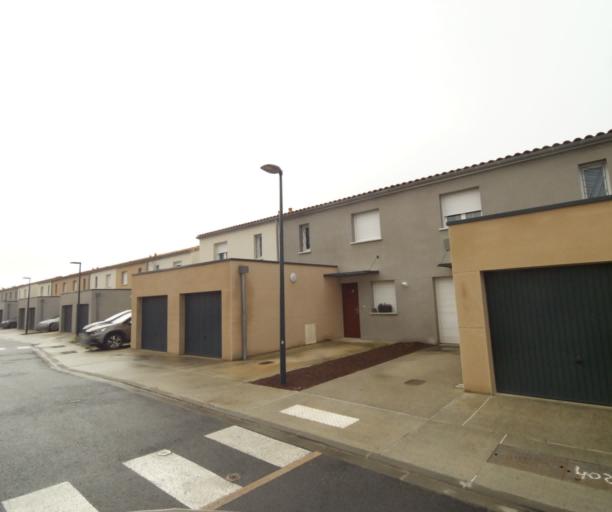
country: FR
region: Midi-Pyrenees
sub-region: Departement de la Haute-Garonne
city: Villemur-sur-Tarn
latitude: 43.8582
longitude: 1.4769
